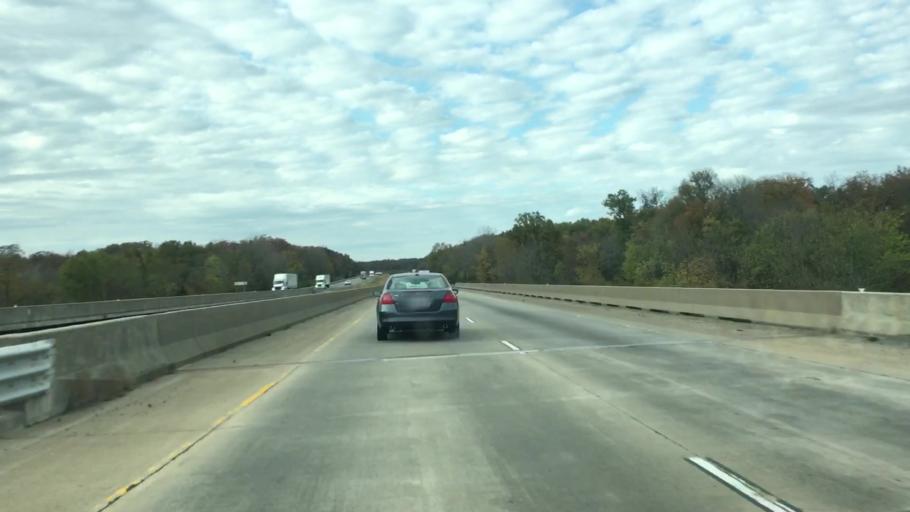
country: US
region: Arkansas
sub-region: Faulkner County
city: Conway
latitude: 35.1301
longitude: -92.5143
